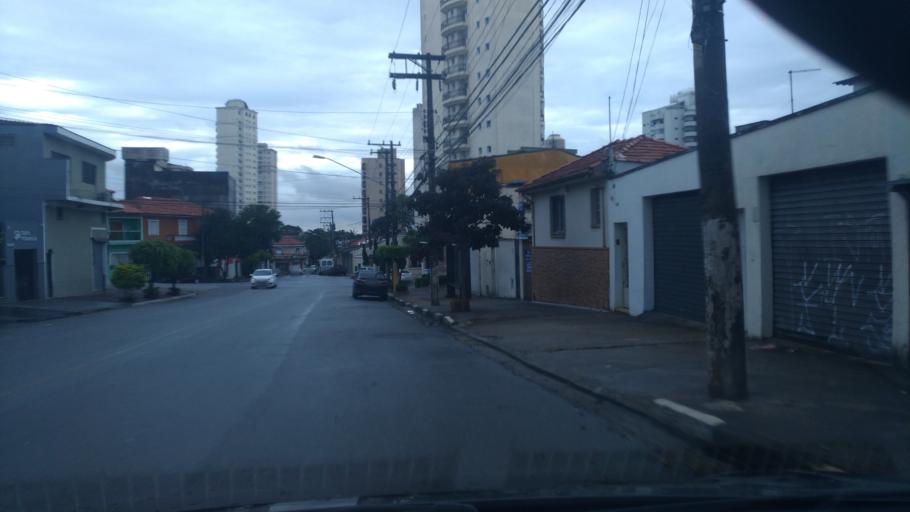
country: BR
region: Sao Paulo
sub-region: Sao Paulo
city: Sao Paulo
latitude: -23.5108
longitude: -46.5849
